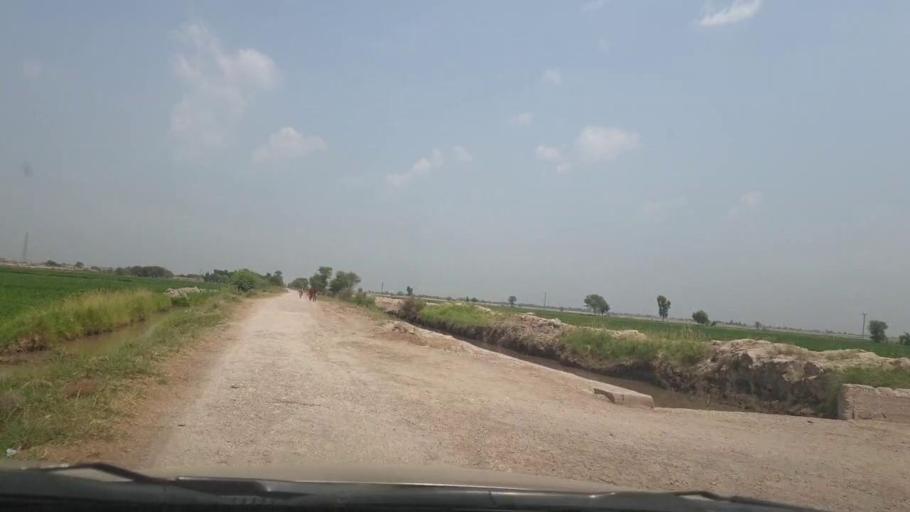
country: PK
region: Sindh
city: Ratodero
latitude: 27.6922
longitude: 68.2331
